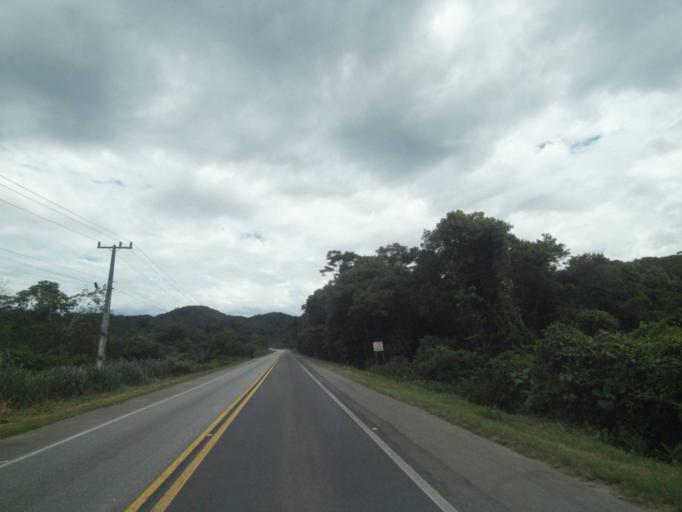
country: BR
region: Parana
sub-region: Antonina
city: Antonina
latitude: -25.4456
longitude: -48.7685
